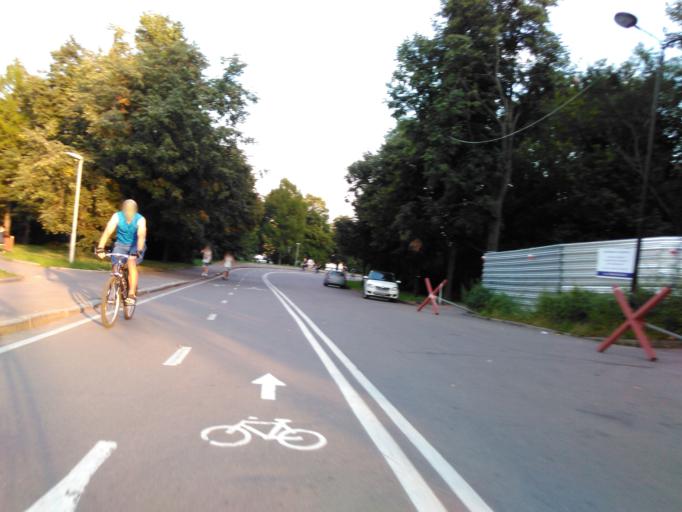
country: RU
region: Moscow
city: Vorob'yovo
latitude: 55.7280
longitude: 37.5414
